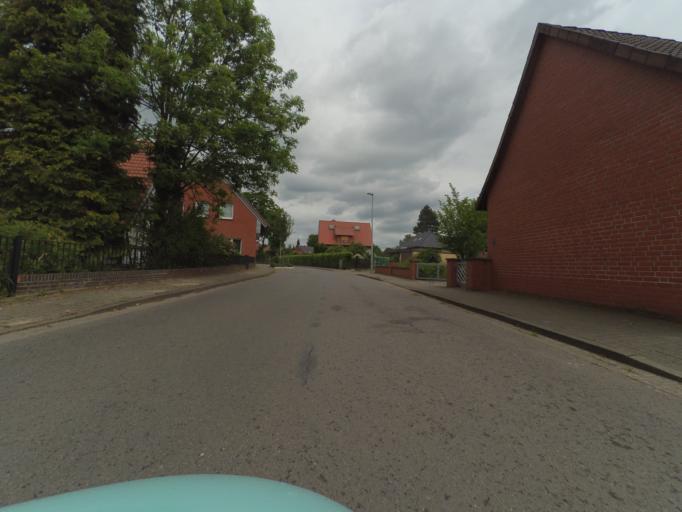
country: DE
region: Lower Saxony
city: Garbsen
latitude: 52.4430
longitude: 9.5667
